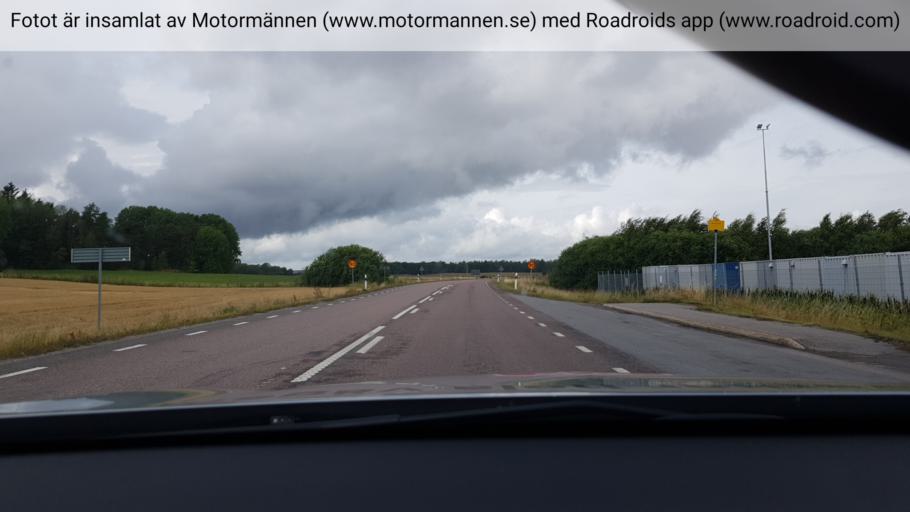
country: SE
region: Uppsala
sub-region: Uppsala Kommun
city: Gamla Uppsala
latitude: 59.8790
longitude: 17.5798
